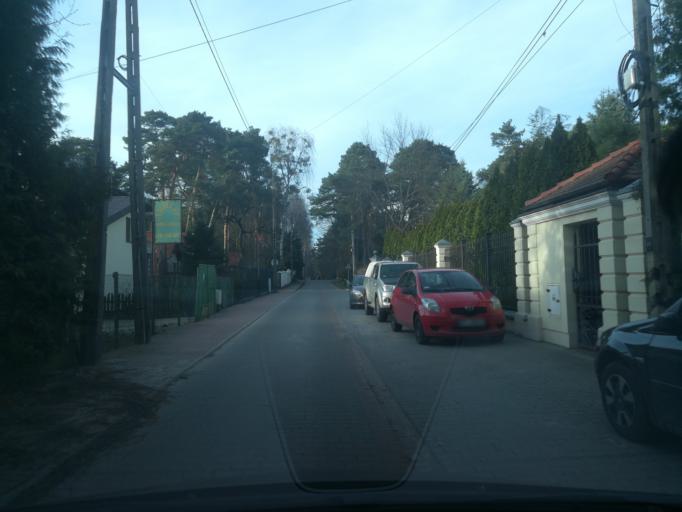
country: PL
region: Masovian Voivodeship
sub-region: Powiat piaseczynski
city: Konstancin-Jeziorna
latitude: 52.0712
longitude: 21.1048
